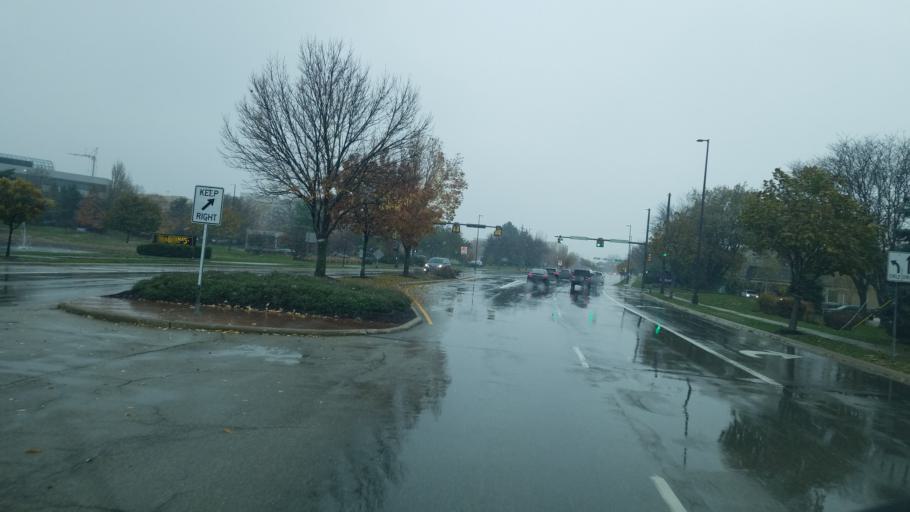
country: US
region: Ohio
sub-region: Franklin County
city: Dublin
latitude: 40.0946
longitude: -83.1250
